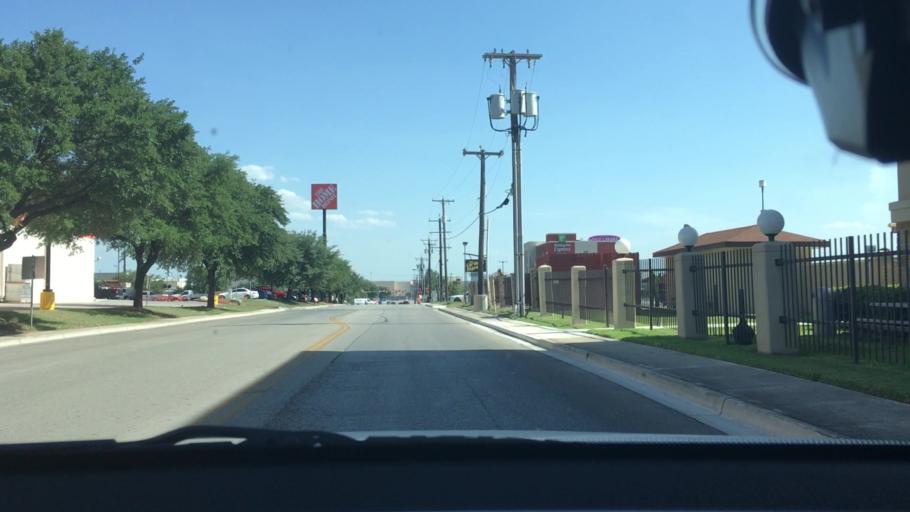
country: US
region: Texas
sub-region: Bexar County
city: Windcrest
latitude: 29.5139
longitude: -98.3951
